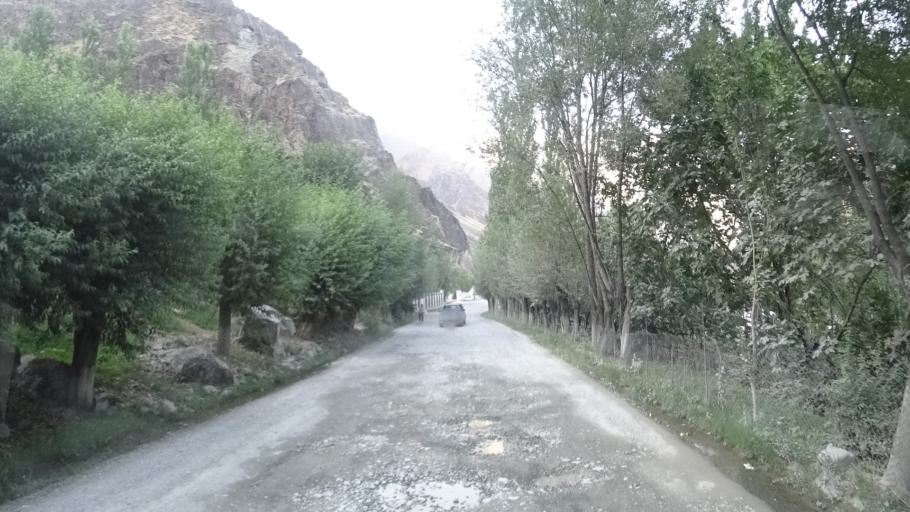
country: TJ
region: Gorno-Badakhshan
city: Qalaikhumb
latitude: 38.4035
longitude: 70.6725
